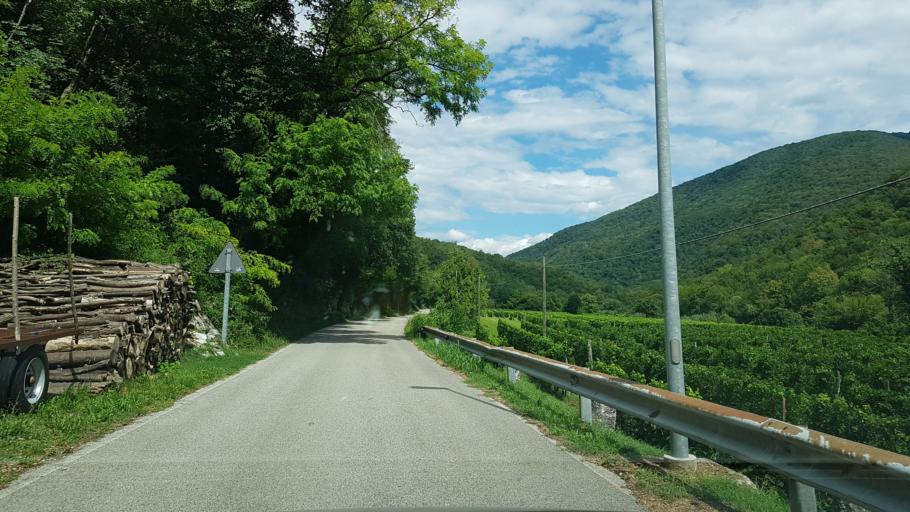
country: IT
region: Friuli Venezia Giulia
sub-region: Provincia di Udine
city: Prepotto
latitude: 46.0645
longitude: 13.5194
